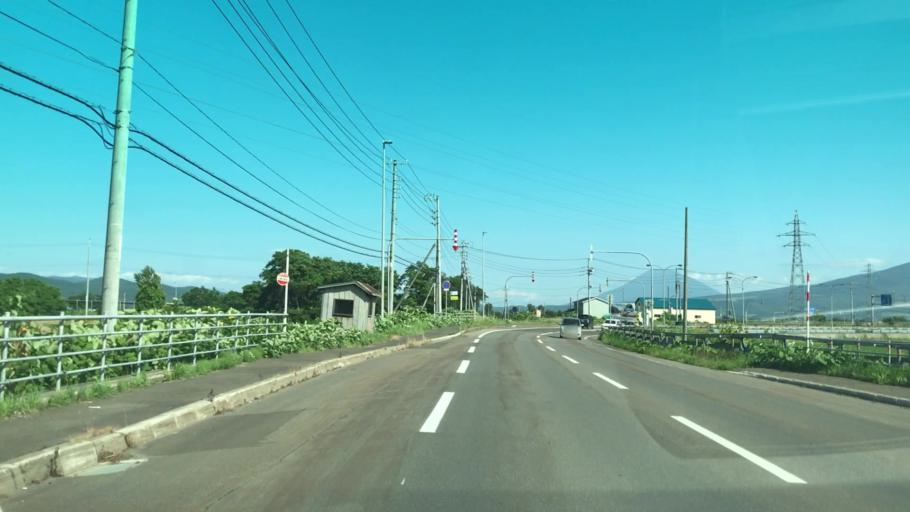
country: JP
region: Hokkaido
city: Iwanai
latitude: 43.0266
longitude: 140.5472
